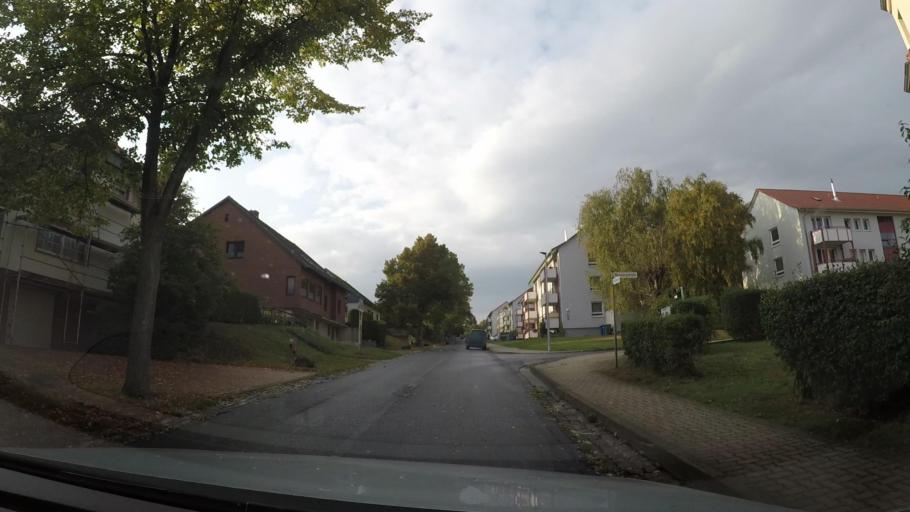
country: DE
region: Lower Saxony
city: Schoningen
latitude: 52.1343
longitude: 10.9622
